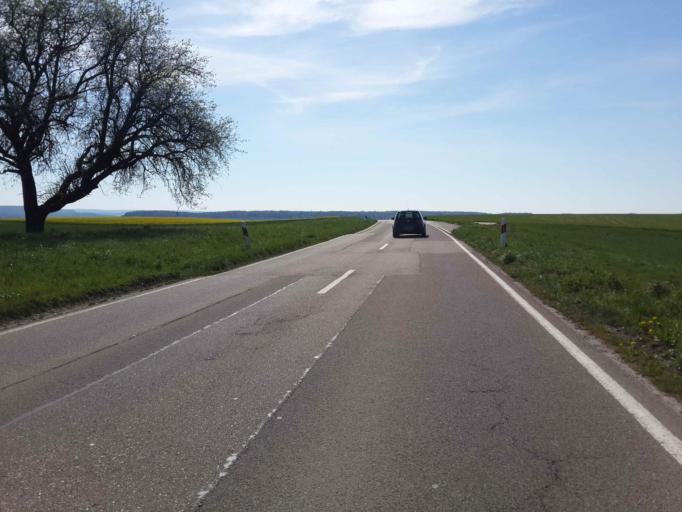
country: DE
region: Baden-Wuerttemberg
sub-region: Regierungsbezirk Stuttgart
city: Massenbachhausen
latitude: 49.1822
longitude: 9.0816
